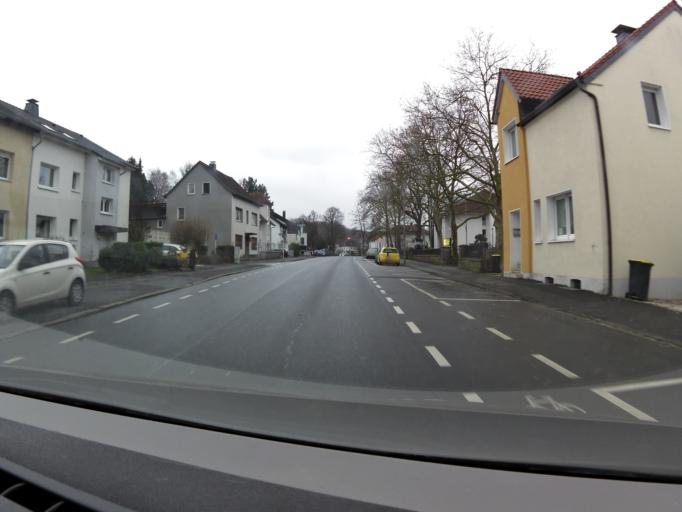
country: DE
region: North Rhine-Westphalia
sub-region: Regierungsbezirk Arnsberg
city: Dortmund
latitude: 51.4636
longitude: 7.4809
